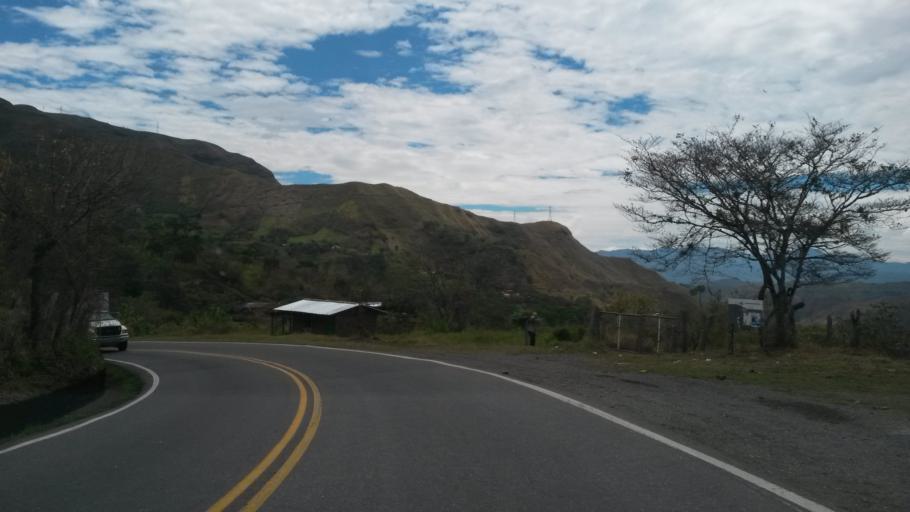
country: CO
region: Cauca
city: Rosas
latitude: 2.2780
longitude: -76.7236
